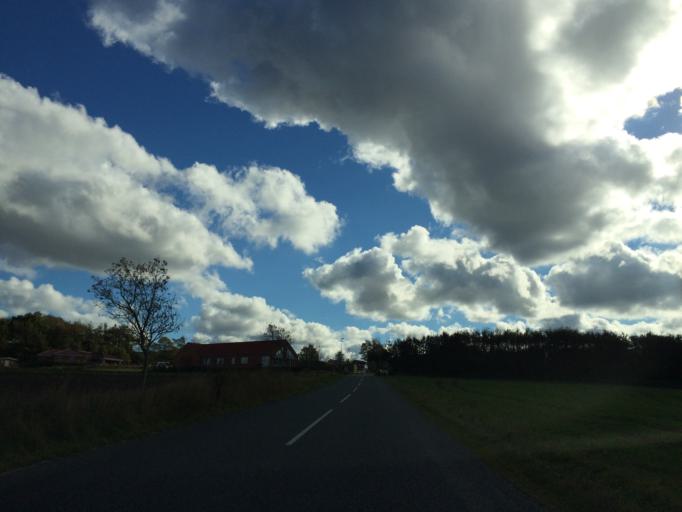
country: DK
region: Central Jutland
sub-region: Skanderborg Kommune
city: Ry
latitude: 56.1825
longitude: 9.7726
